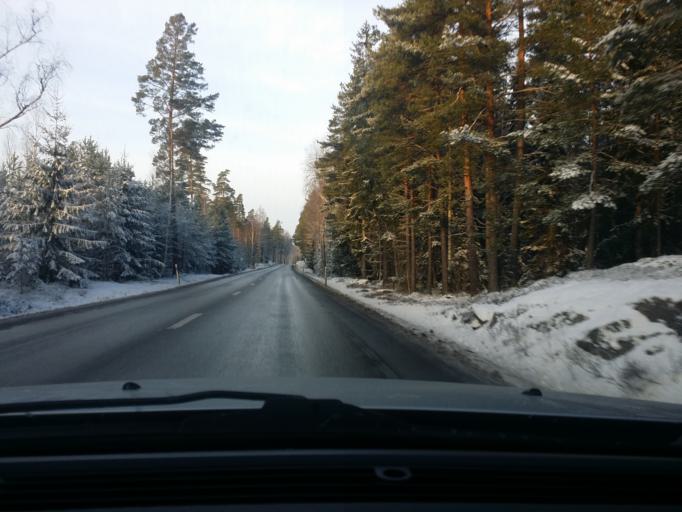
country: SE
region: OErebro
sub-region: Lindesbergs Kommun
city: Frovi
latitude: 59.5104
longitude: 15.3532
